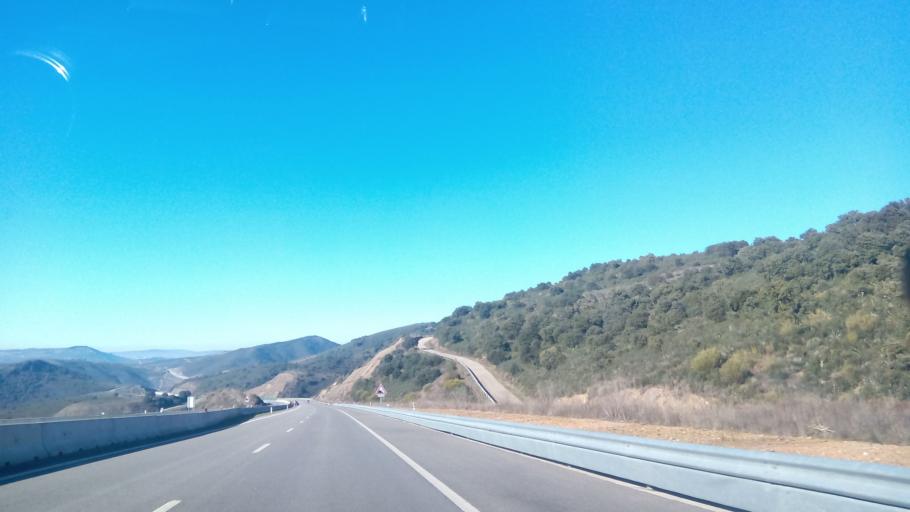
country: PT
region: Braganca
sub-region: Braganca Municipality
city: Braganca
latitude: 41.7641
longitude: -6.6524
